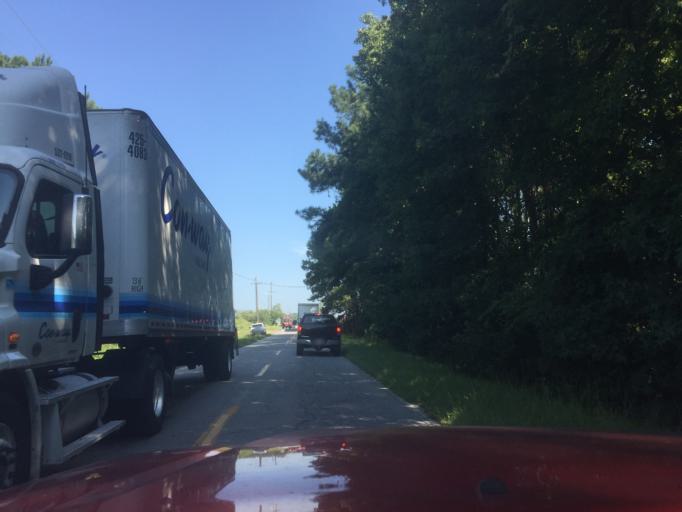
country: US
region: Georgia
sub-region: Chatham County
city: Garden City
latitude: 32.0753
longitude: -81.1435
